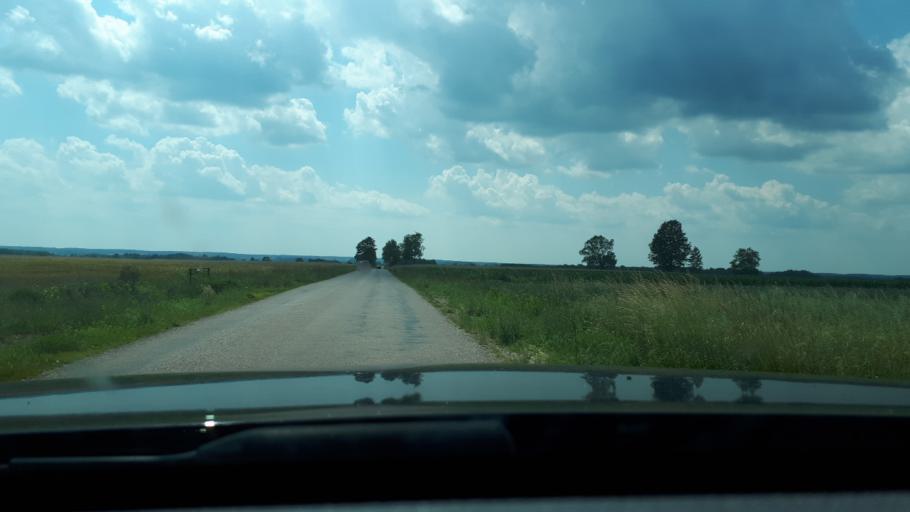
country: PL
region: Podlasie
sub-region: Powiat bialostocki
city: Lapy
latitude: 53.0970
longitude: 22.8592
